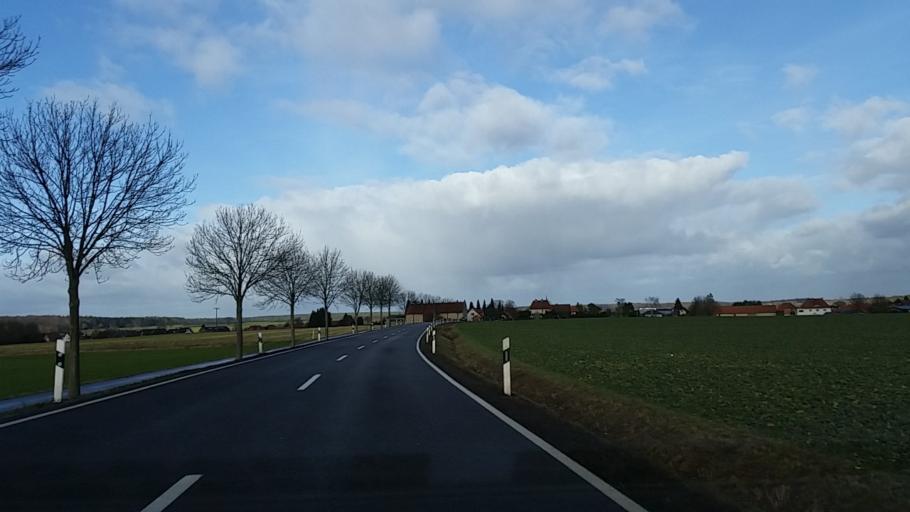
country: DE
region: Lower Saxony
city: Gross Twulpstedt
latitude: 52.3801
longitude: 10.9198
